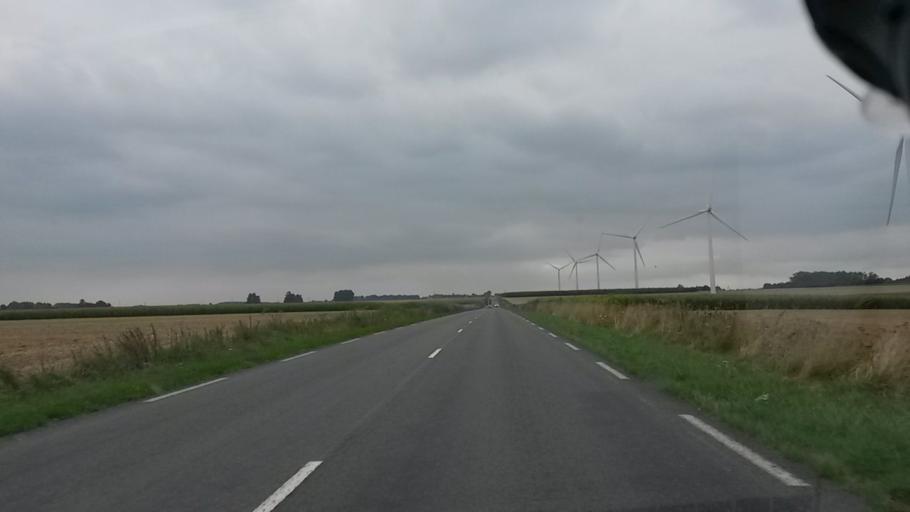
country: FR
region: Haute-Normandie
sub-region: Departement de la Seine-Maritime
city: Aumale
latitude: 49.7721
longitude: 1.8431
